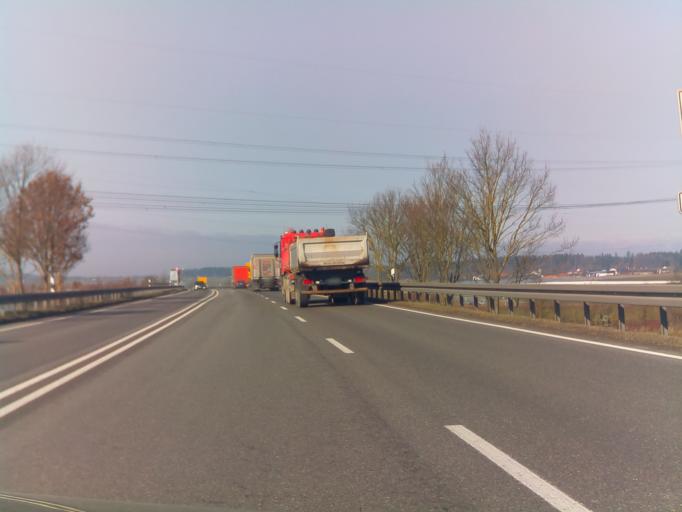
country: DE
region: Baden-Wuerttemberg
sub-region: Regierungsbezirk Stuttgart
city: Bondorf
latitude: 48.5068
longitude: 8.8252
